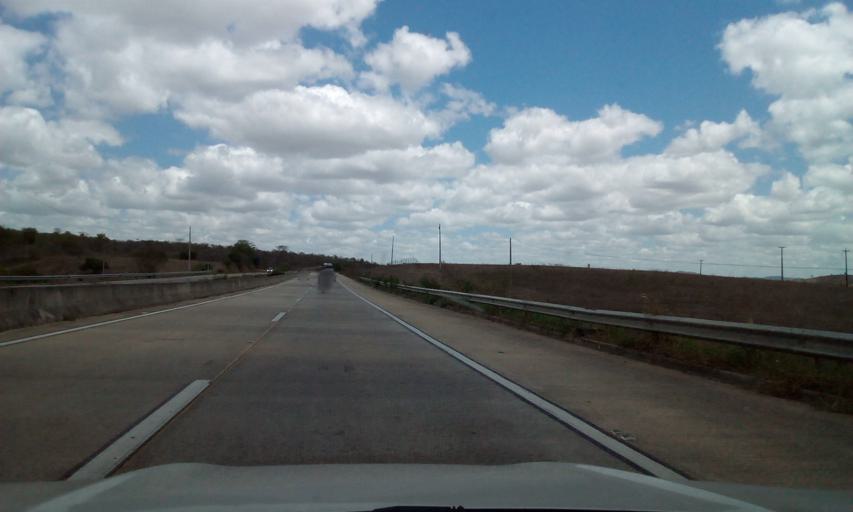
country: BR
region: Alagoas
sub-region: Porto Real Do Colegio
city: Porto Real do Colegio
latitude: -10.1577
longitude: -36.8120
